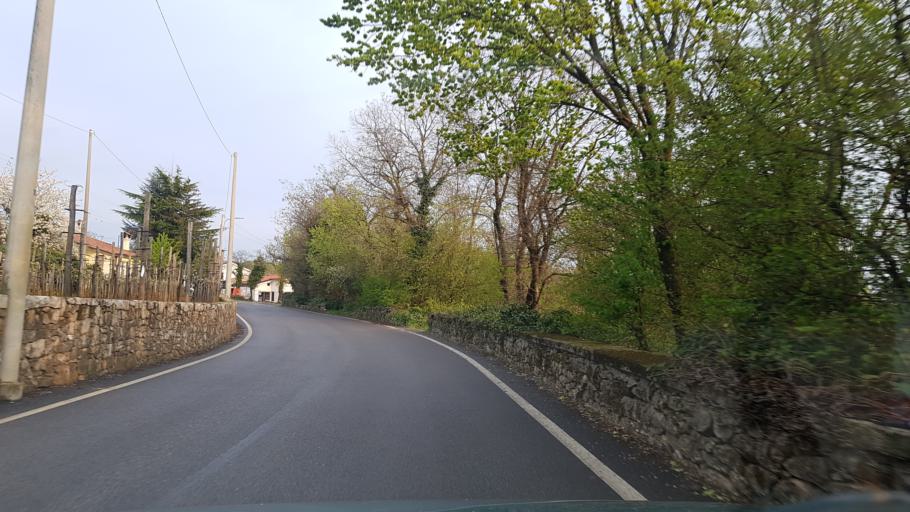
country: IT
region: Friuli Venezia Giulia
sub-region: Provincia di Trieste
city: Sgonico
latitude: 45.7449
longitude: 13.7350
